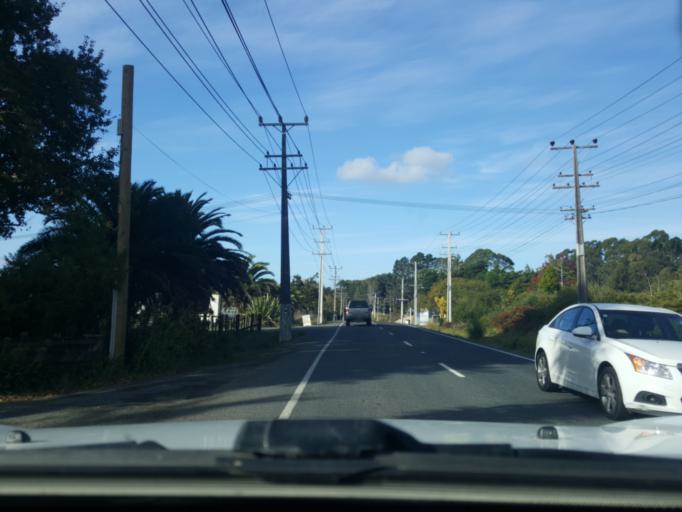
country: NZ
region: Auckland
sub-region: Auckland
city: Muriwai Beach
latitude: -36.7622
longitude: 174.5781
